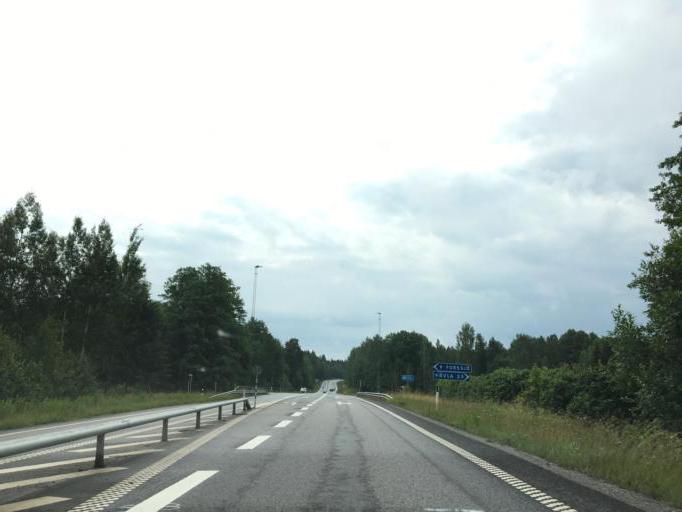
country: SE
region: Soedermanland
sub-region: Katrineholms Kommun
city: Katrineholm
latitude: 58.9059
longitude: 16.2008
